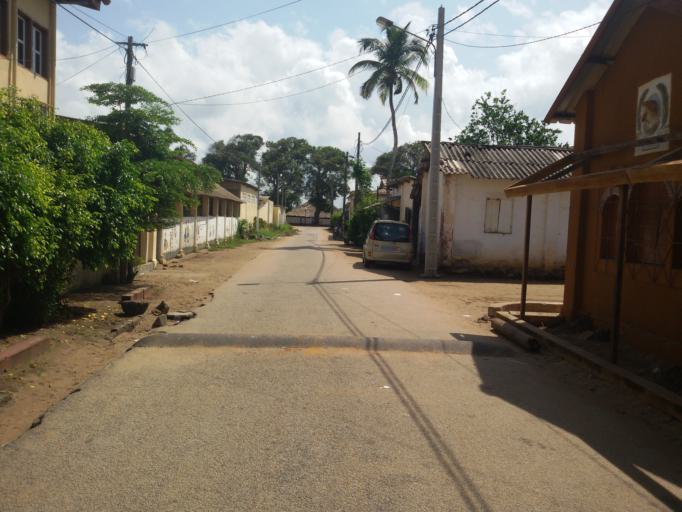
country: CI
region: Sud-Comoe
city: Grand-Bassam
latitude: 5.1958
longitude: -3.7340
